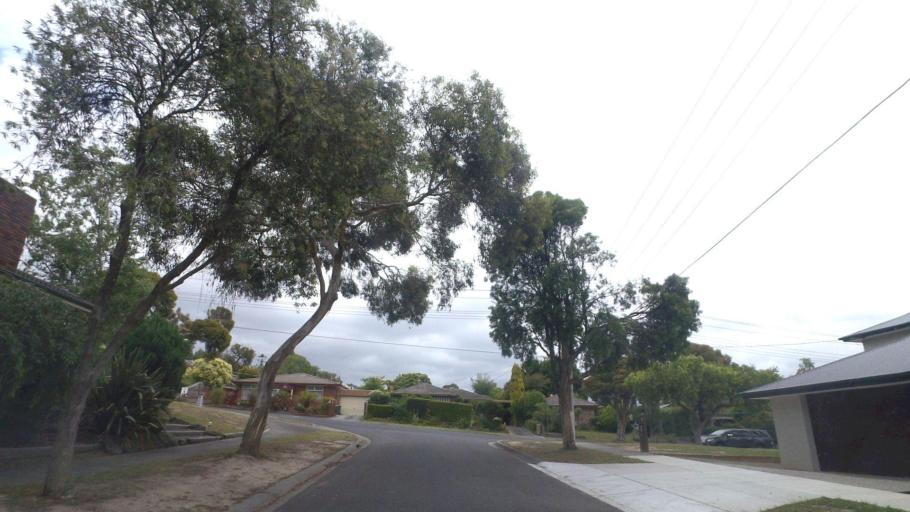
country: AU
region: Victoria
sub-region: Knox
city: The Basin
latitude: -37.8548
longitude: 145.3074
